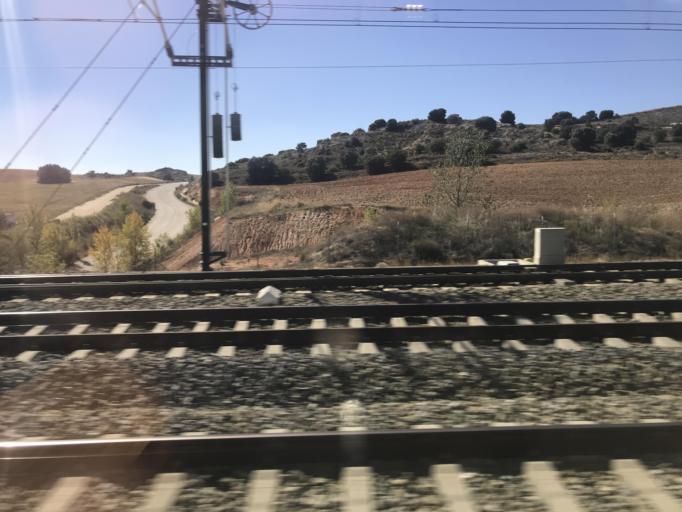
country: ES
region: Castille-La Mancha
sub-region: Provincia de Cuenca
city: Cuenca
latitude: 40.0312
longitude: -2.1397
